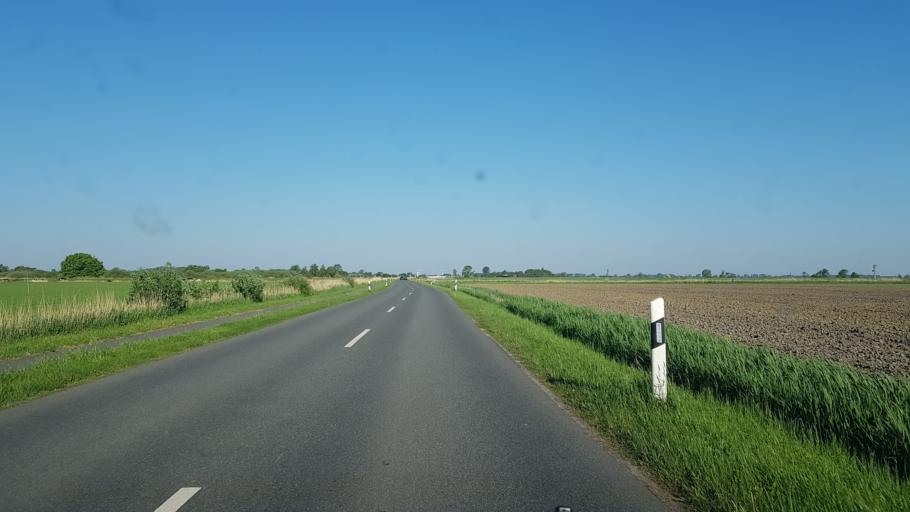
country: DE
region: Lower Saxony
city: Langen
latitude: 53.6119
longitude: 8.5657
